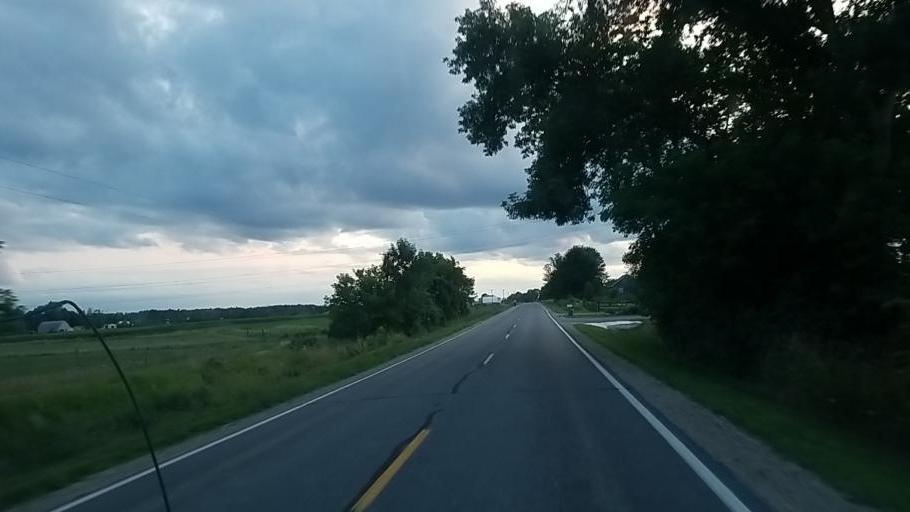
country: US
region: Michigan
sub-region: Newaygo County
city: Fremont
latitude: 43.4675
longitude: -86.0467
